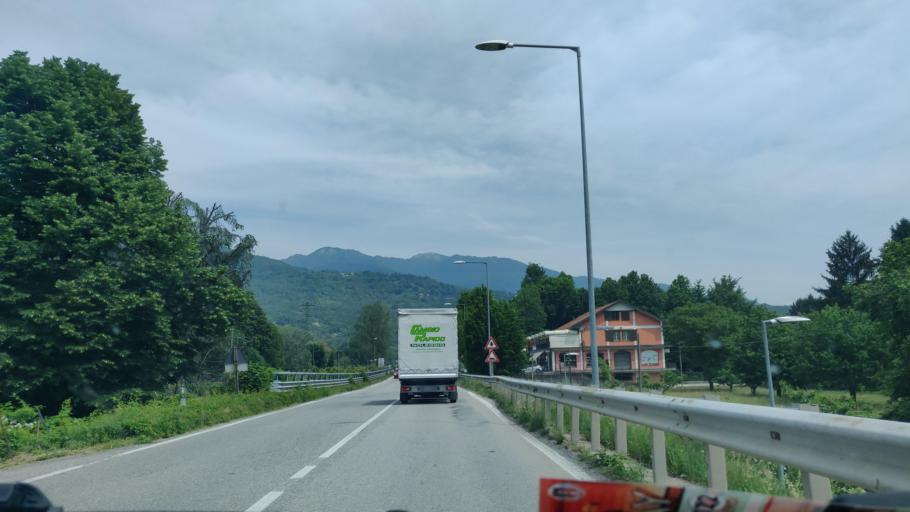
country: IT
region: Piedmont
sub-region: Provincia Verbano-Cusio-Ossola
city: Baveno
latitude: 45.9372
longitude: 8.4833
